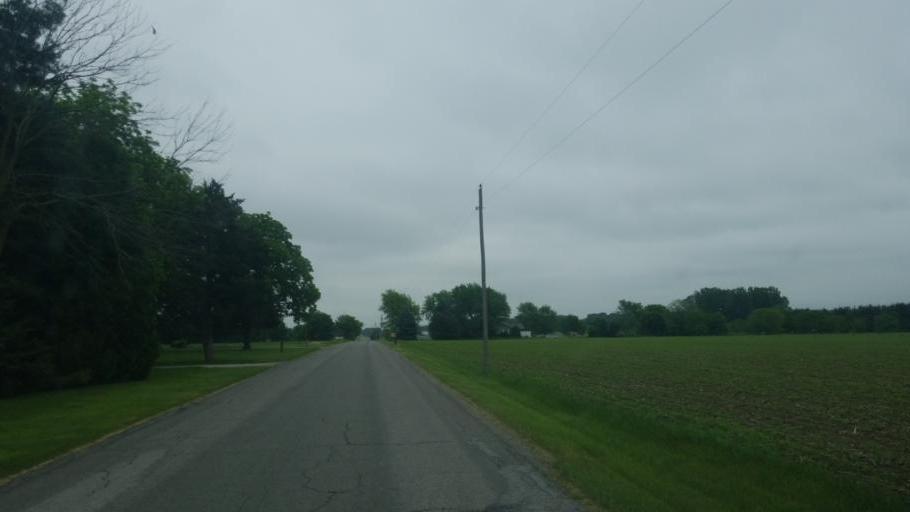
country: US
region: Indiana
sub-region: Elkhart County
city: Nappanee
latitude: 41.4717
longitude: -86.0486
